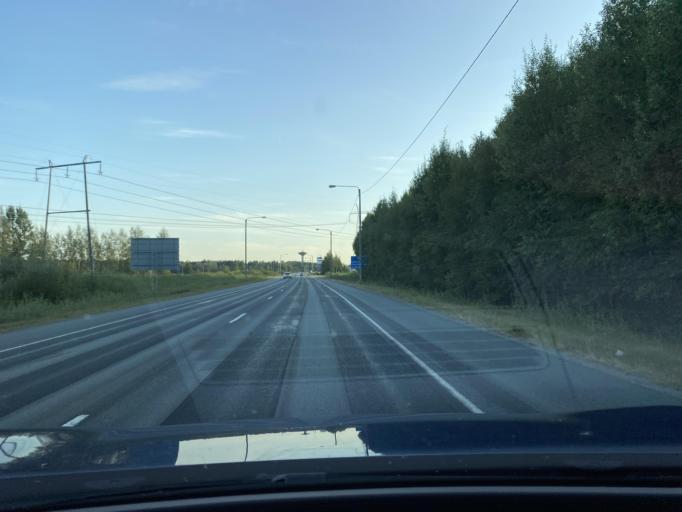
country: FI
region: Southern Ostrobothnia
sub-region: Seinaejoki
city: Nurmo
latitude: 62.8164
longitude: 22.9009
